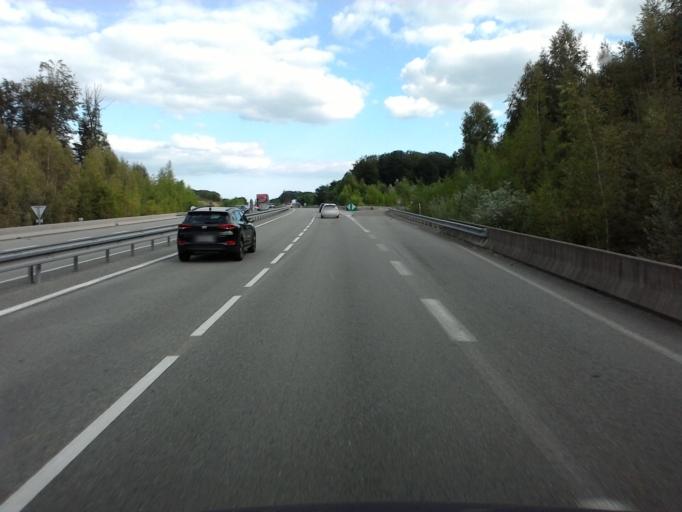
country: FR
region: Franche-Comte
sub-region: Departement de la Haute-Saone
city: Luxeuil-les-Bains
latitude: 47.8509
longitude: 6.3851
